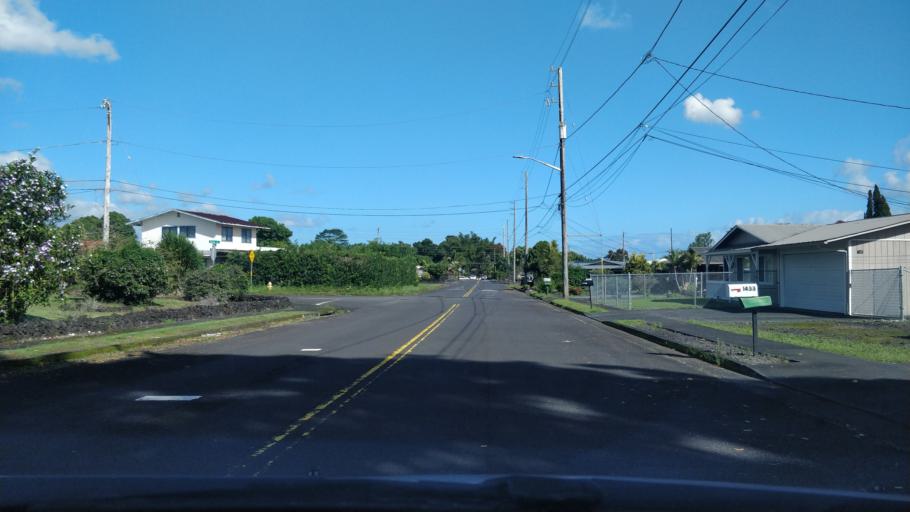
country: US
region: Hawaii
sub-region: Hawaii County
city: Hilo
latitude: 19.6811
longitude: -155.0867
